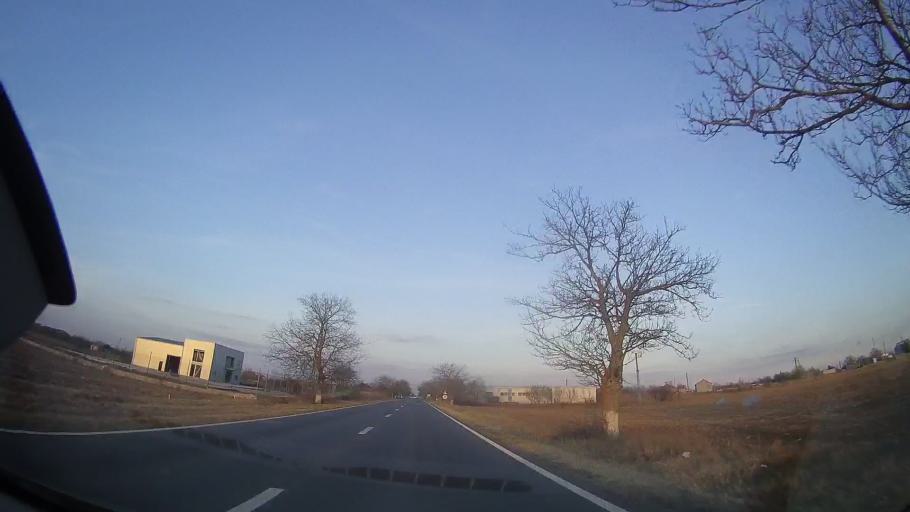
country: RO
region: Constanta
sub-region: Comuna Topraisar
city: Topraisar
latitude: 44.0063
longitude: 28.4420
